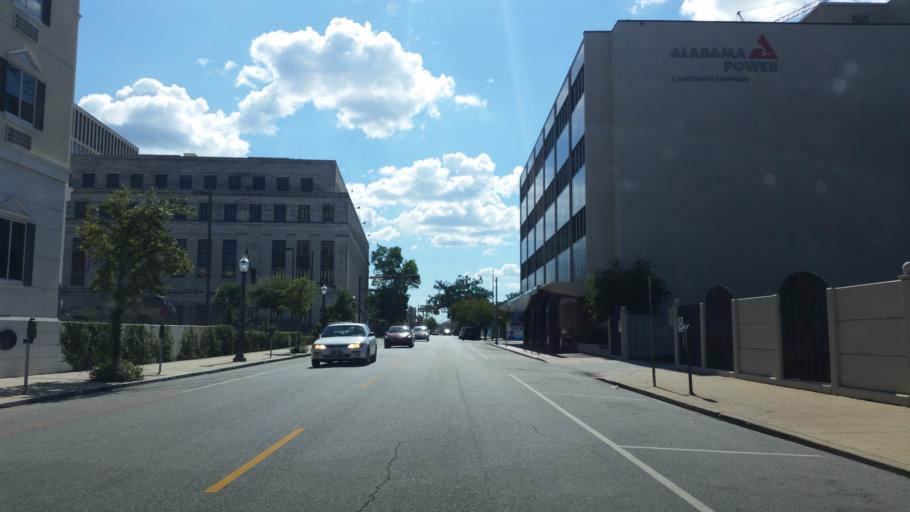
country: US
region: Alabama
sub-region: Mobile County
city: Mobile
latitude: 30.6947
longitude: -88.0421
